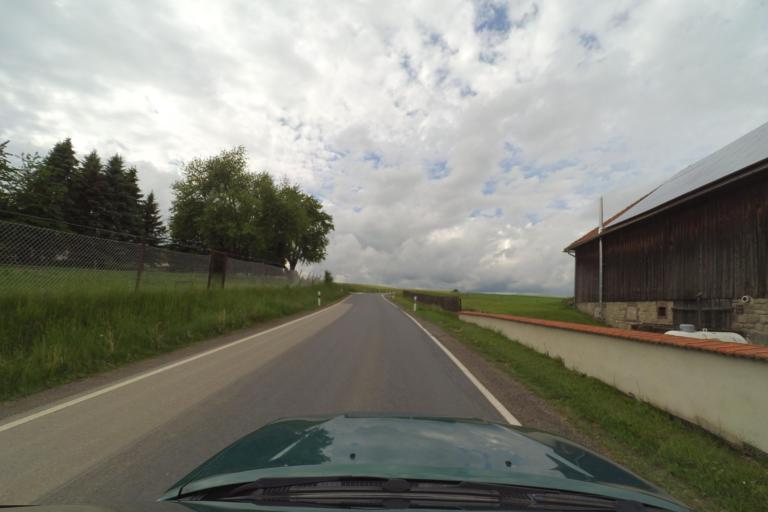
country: DE
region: Bavaria
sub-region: Upper Palatinate
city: Floss
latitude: 49.6929
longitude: 12.2896
